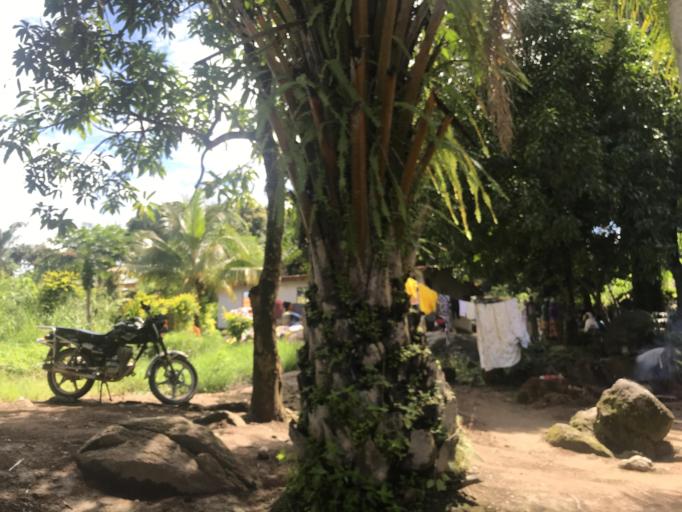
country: SL
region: Eastern Province
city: Koidu
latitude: 8.6466
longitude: -10.9897
